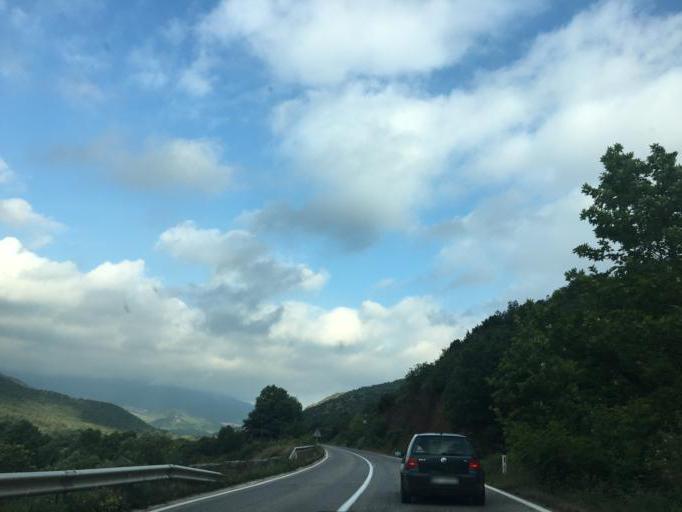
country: MK
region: Demir Kapija
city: Demir Kapija
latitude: 41.3907
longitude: 22.3547
